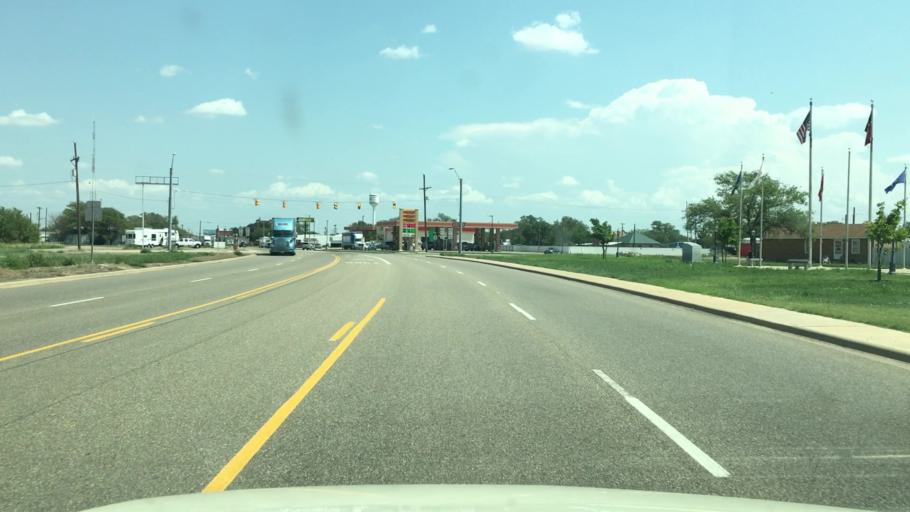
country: US
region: Texas
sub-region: Armstrong County
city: Claude
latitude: 35.1124
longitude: -101.3647
